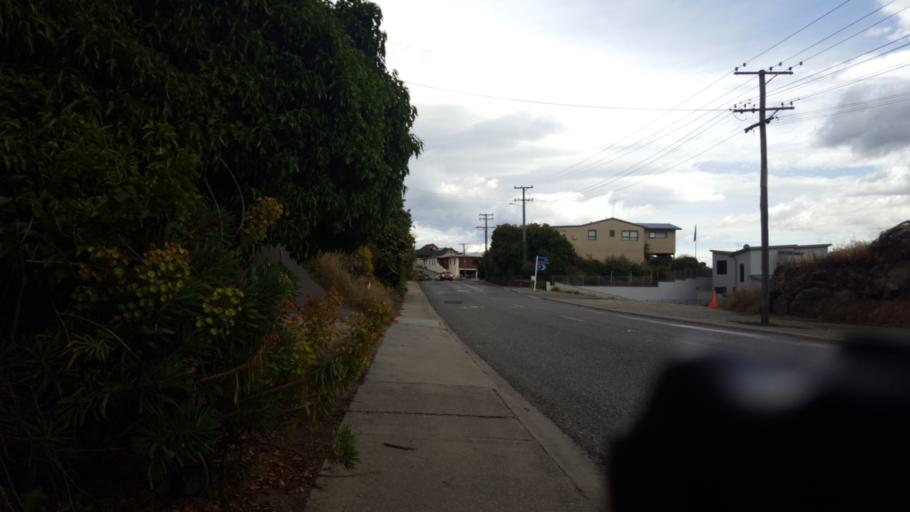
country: NZ
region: Otago
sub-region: Queenstown-Lakes District
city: Wanaka
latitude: -45.2591
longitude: 169.3855
